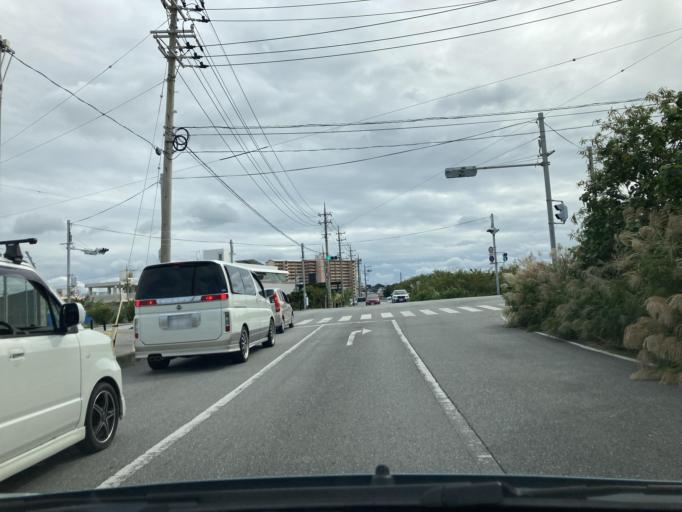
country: JP
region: Okinawa
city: Itoman
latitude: 26.1547
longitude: 127.6679
